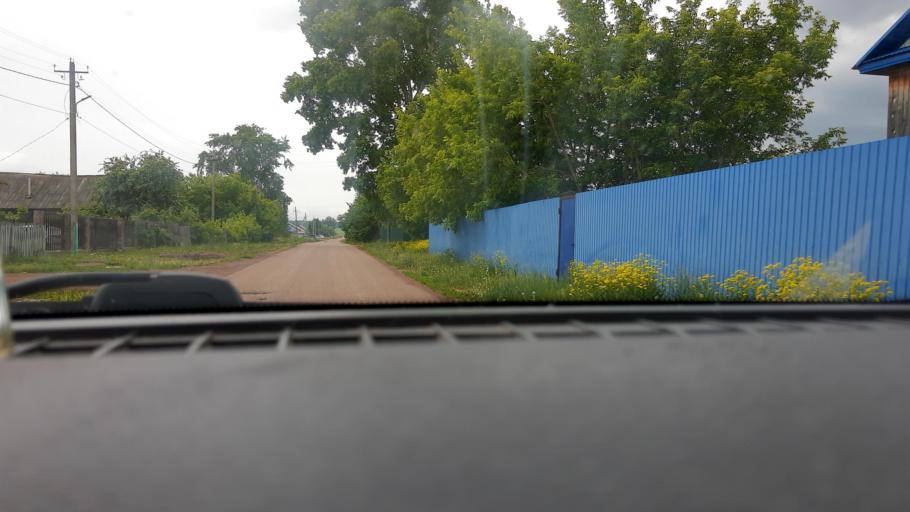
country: RU
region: Bashkortostan
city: Dmitriyevka
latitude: 54.7236
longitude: 55.4971
